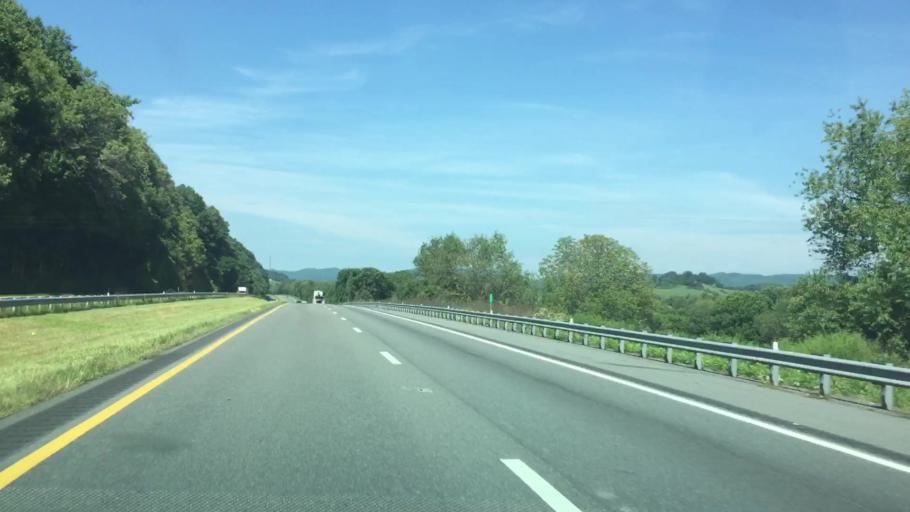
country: US
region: Virginia
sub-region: Smyth County
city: Chilhowie
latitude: 36.8089
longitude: -81.6343
